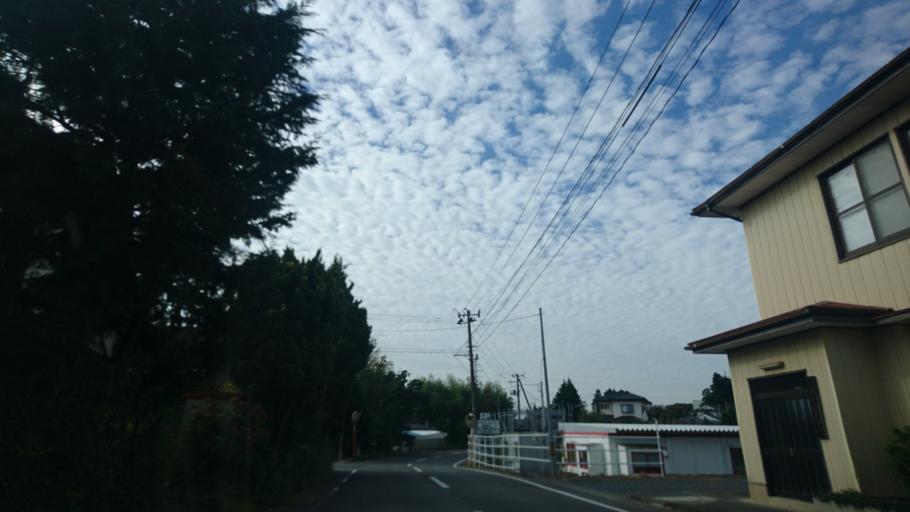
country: JP
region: Fukushima
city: Sukagawa
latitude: 37.3410
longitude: 140.3549
